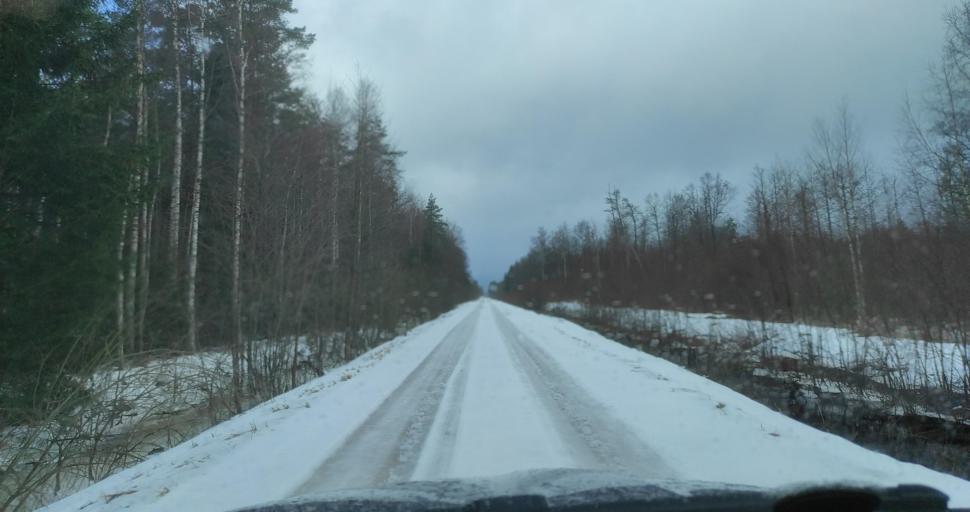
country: LV
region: Dundaga
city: Dundaga
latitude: 57.3964
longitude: 22.1177
